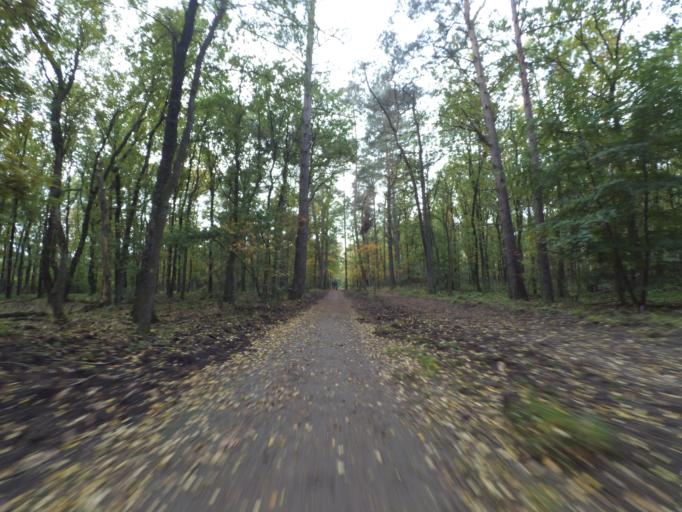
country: NL
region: Gelderland
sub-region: Gemeente Ermelo
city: Ermelo
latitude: 52.3068
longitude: 5.6618
